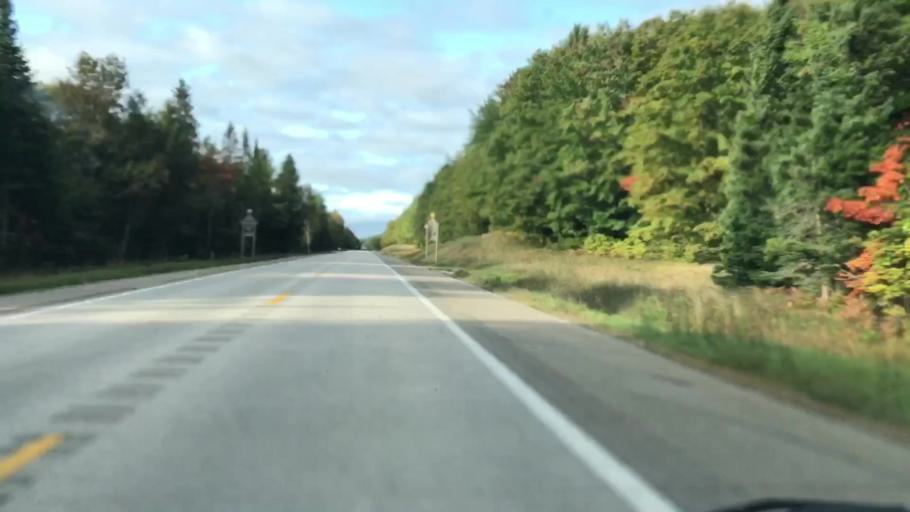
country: US
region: Michigan
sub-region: Luce County
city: Newberry
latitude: 46.3422
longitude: -85.0374
